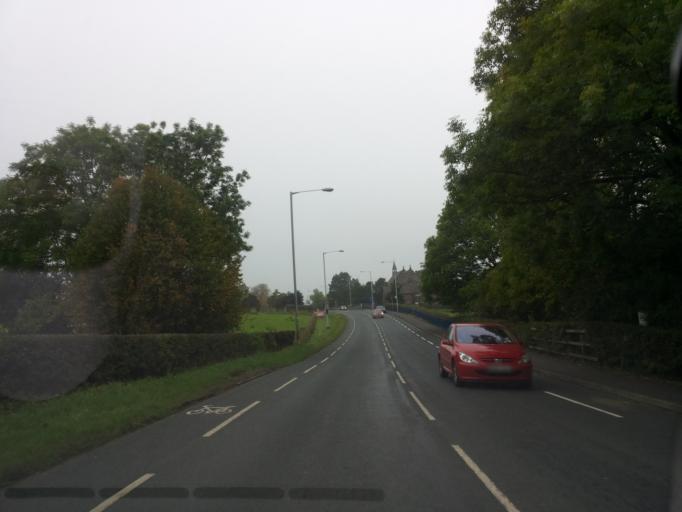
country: GB
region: England
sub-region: Lancashire
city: Billington
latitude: 53.8102
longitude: -2.4359
